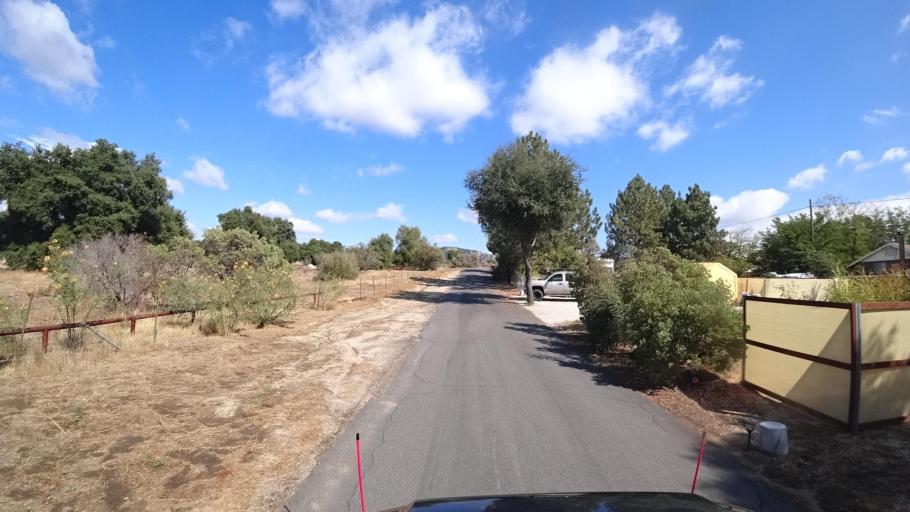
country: US
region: California
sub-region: San Diego County
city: Campo
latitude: 32.6822
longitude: -116.5091
